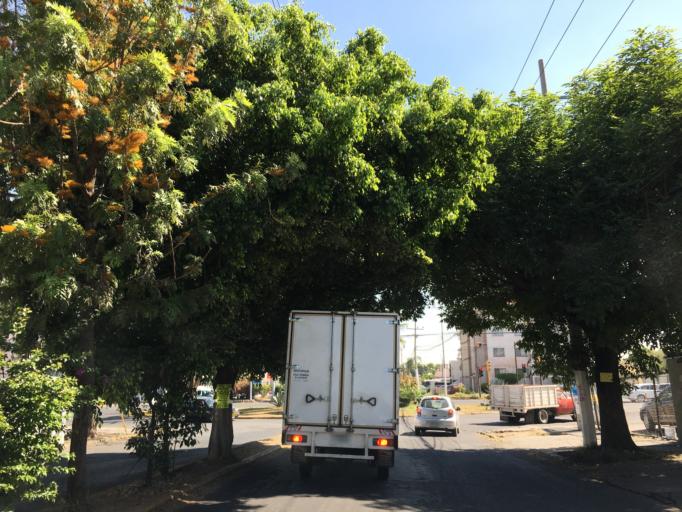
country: MX
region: Jalisco
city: Guadalajara
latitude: 20.6253
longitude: -103.4140
